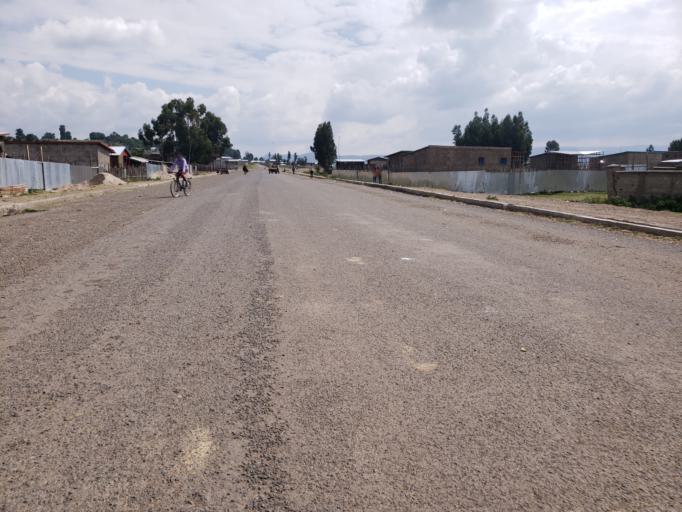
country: ET
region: Oromiya
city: Dodola
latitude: 6.9995
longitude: 39.3916
